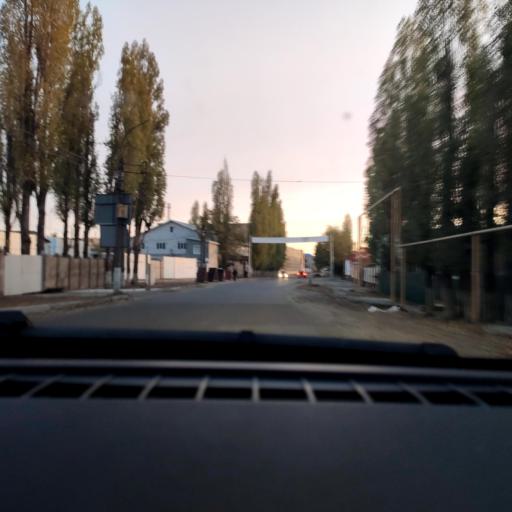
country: RU
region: Voronezj
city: Voronezh
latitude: 51.6527
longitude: 39.2816
